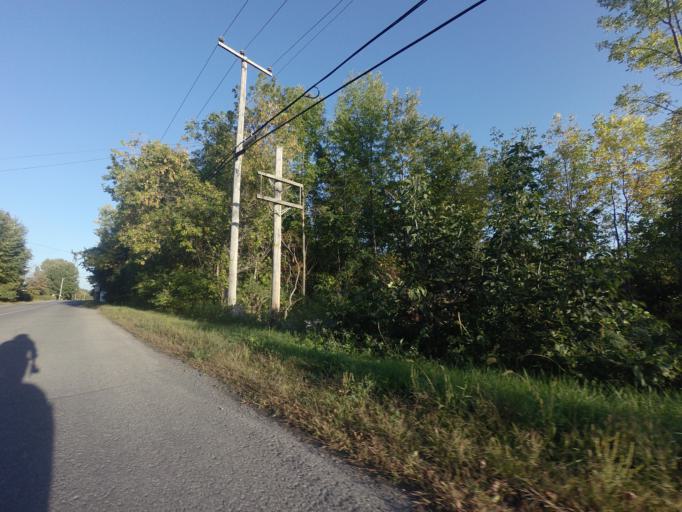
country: CA
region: Quebec
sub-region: Monteregie
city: Rigaud
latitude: 45.4807
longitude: -74.2526
